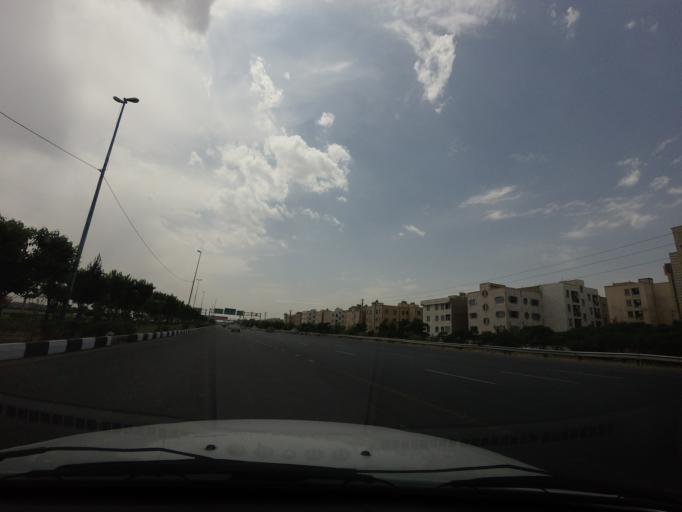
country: IR
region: Tehran
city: Eslamshahr
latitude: 35.5293
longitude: 51.2317
